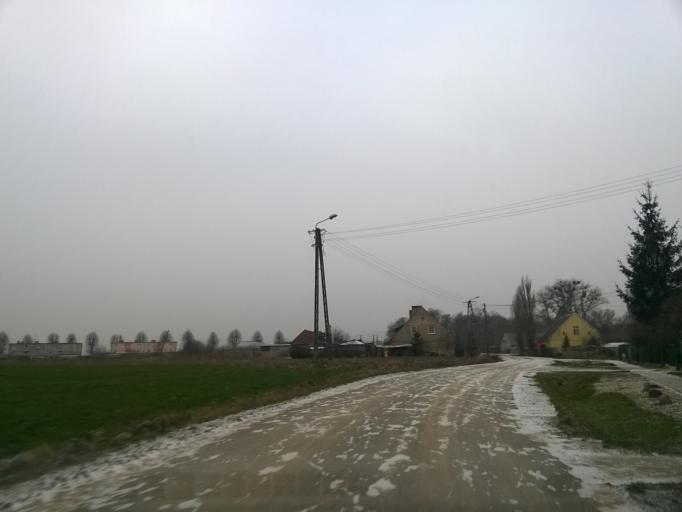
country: PL
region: Kujawsko-Pomorskie
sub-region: Powiat nakielski
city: Kcynia
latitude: 53.0112
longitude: 17.5025
